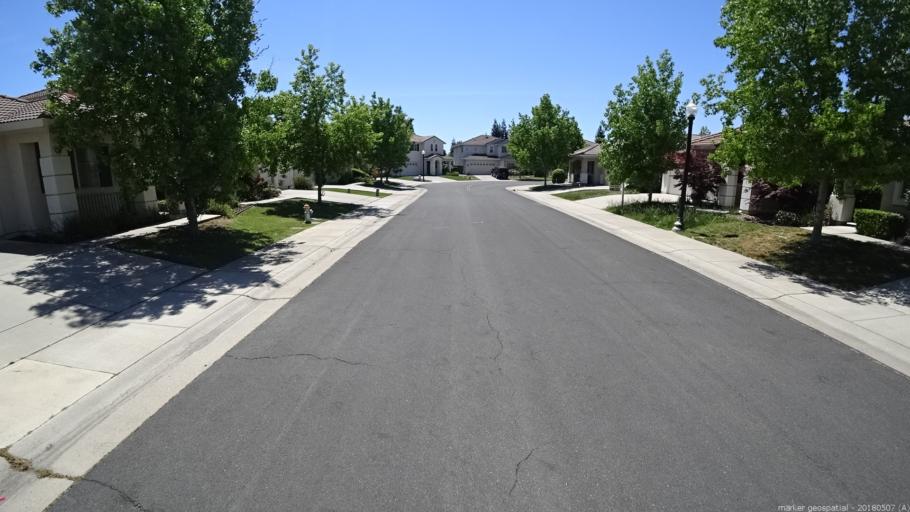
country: US
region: California
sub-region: Sacramento County
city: Elverta
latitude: 38.6758
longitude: -121.5125
